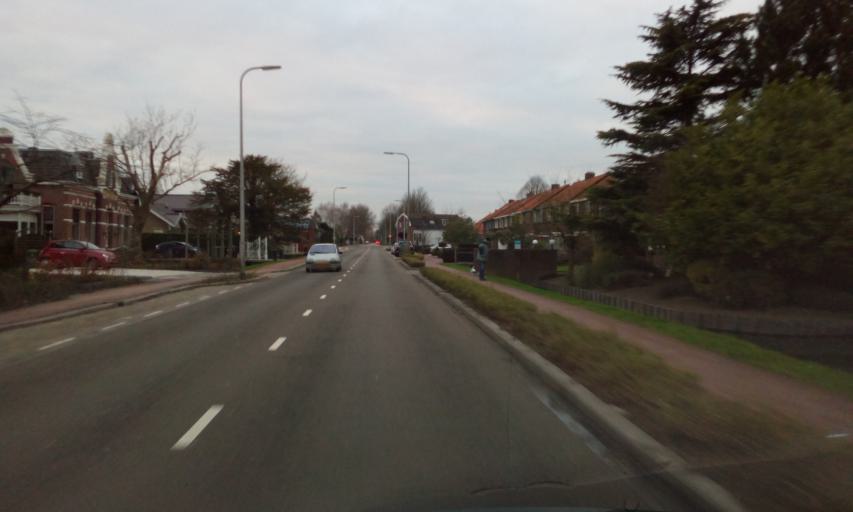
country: NL
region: South Holland
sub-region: Gemeente Ridderkerk
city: Ridderkerk
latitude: 51.8535
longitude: 4.5884
